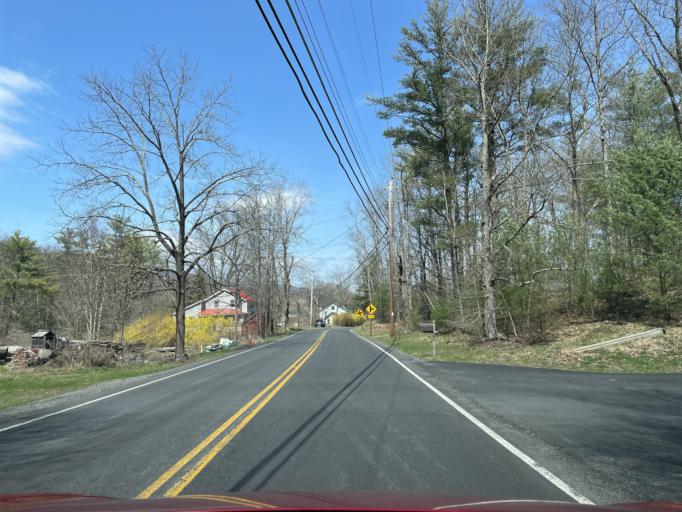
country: US
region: New York
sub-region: Ulster County
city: Manorville
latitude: 42.1072
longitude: -74.0196
